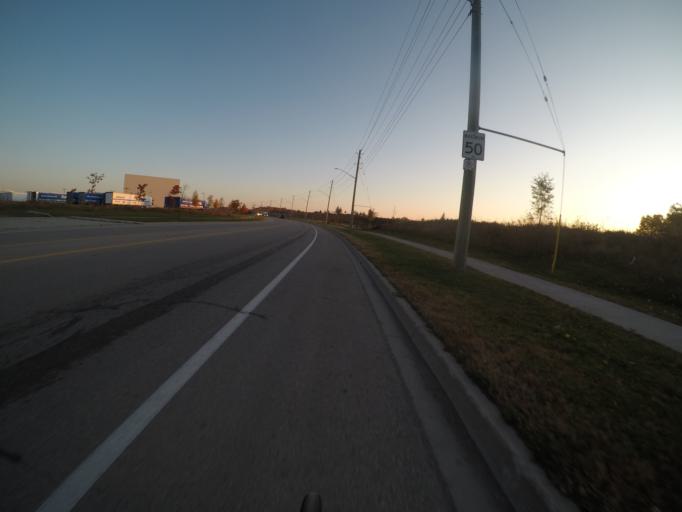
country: CA
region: Ontario
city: Kitchener
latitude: 43.4110
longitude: -80.4346
